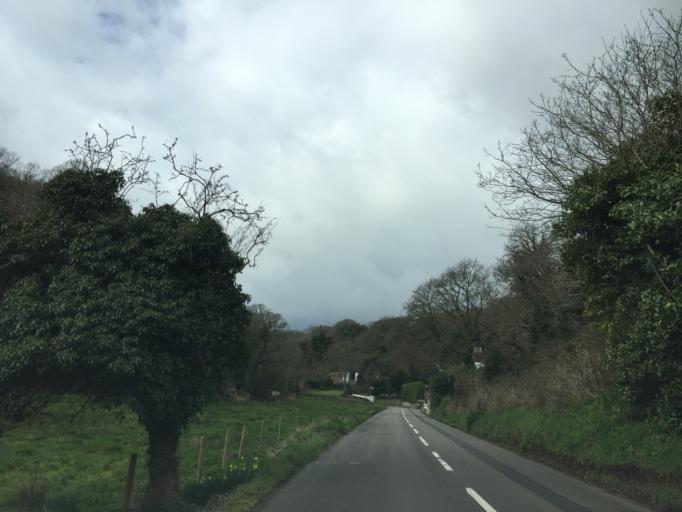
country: JE
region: St Helier
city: Saint Helier
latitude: 49.2115
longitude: -2.1625
